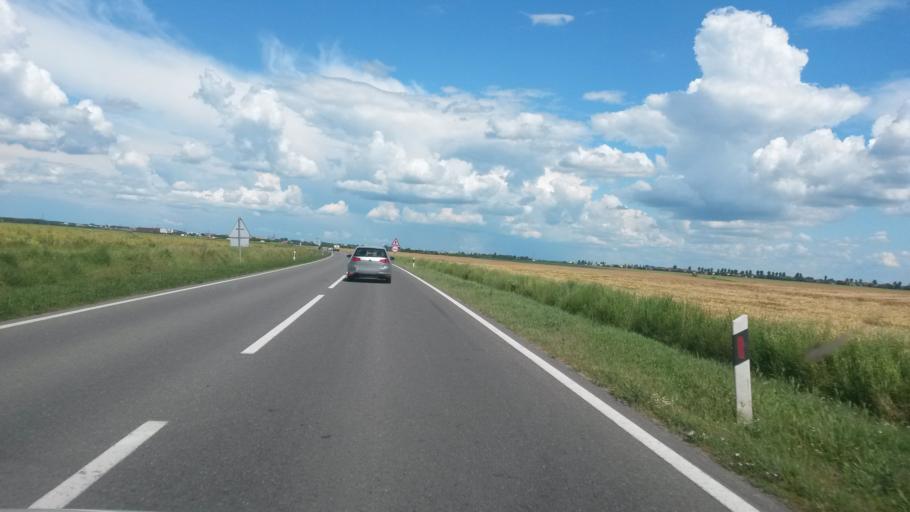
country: HR
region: Osjecko-Baranjska
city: Visnjevac
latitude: 45.5415
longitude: 18.6017
